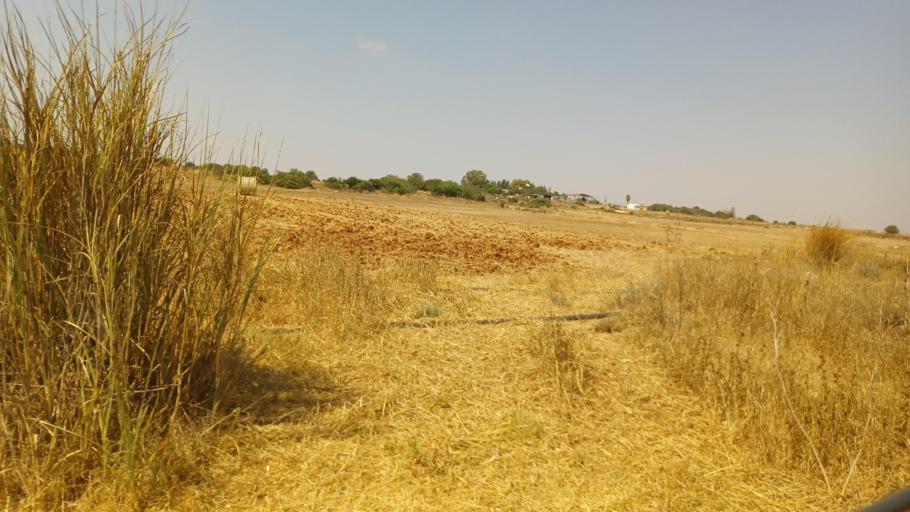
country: CY
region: Ammochostos
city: Frenaros
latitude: 35.0628
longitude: 33.9182
